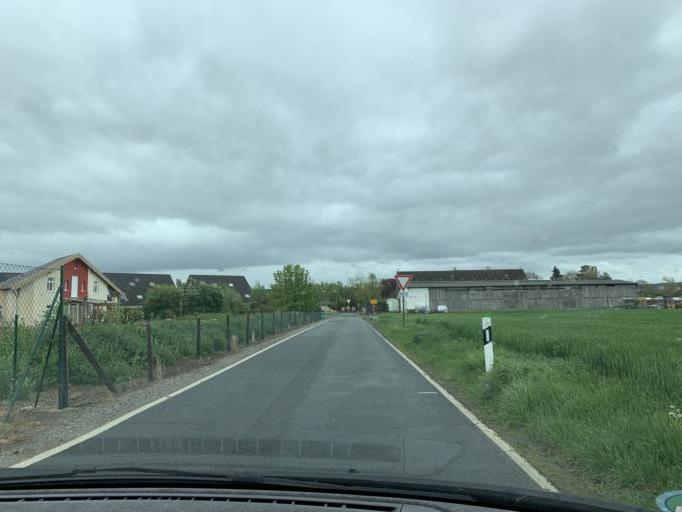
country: DE
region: North Rhine-Westphalia
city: Zulpich
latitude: 50.6559
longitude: 6.6915
